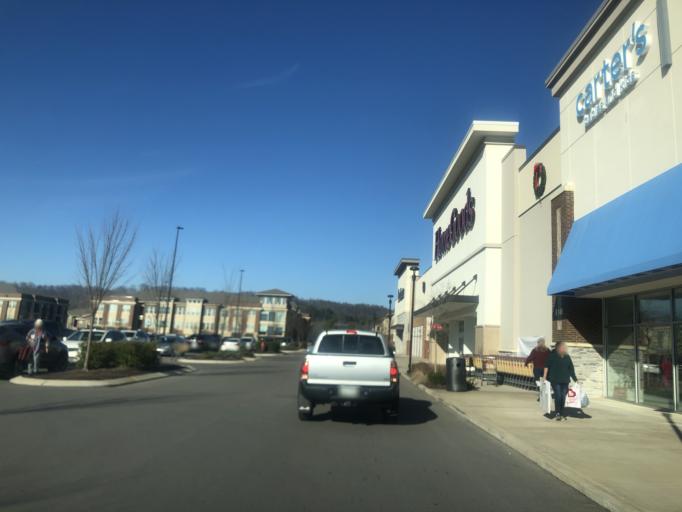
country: US
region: Tennessee
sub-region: Davidson County
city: Belle Meade
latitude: 36.0809
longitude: -86.9458
